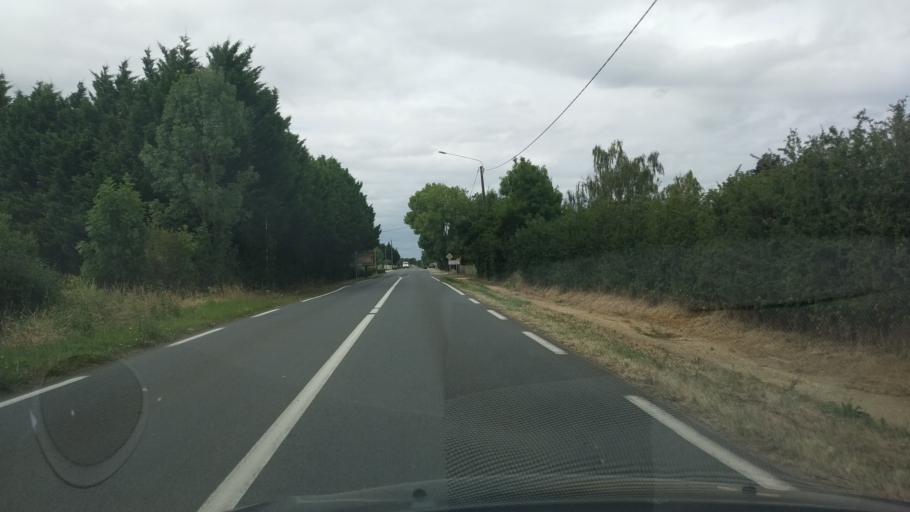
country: FR
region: Poitou-Charentes
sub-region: Departement de la Vienne
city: La Villedieu-du-Clain
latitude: 46.4481
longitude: 0.3691
